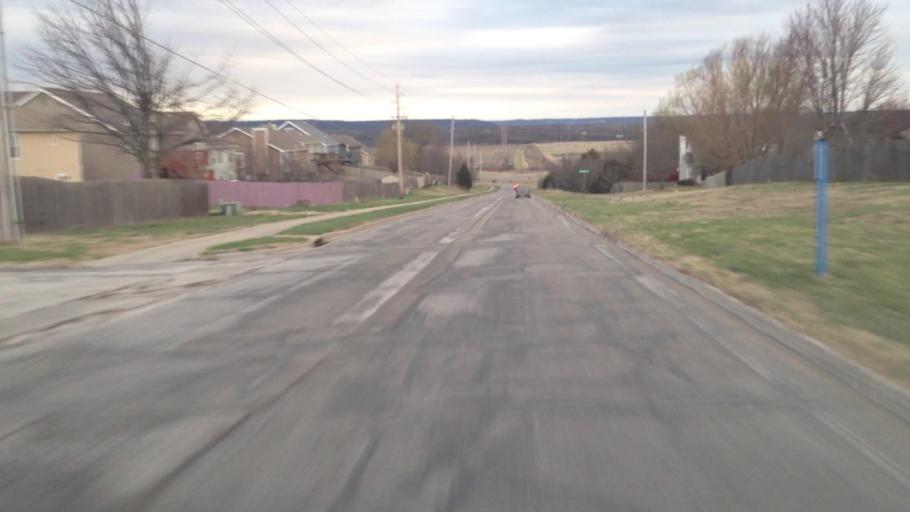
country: US
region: Kansas
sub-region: Douglas County
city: Lawrence
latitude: 38.9405
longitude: -95.3073
